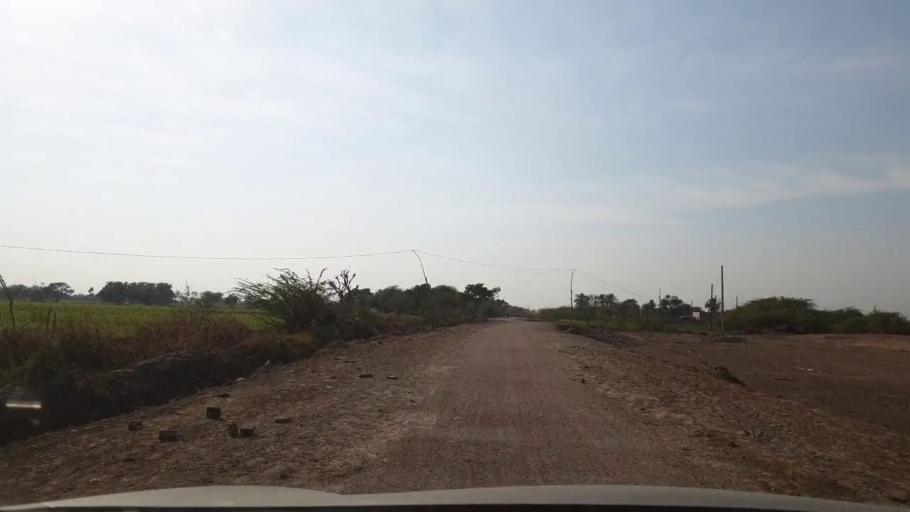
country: PK
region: Sindh
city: Berani
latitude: 25.7126
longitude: 68.8058
